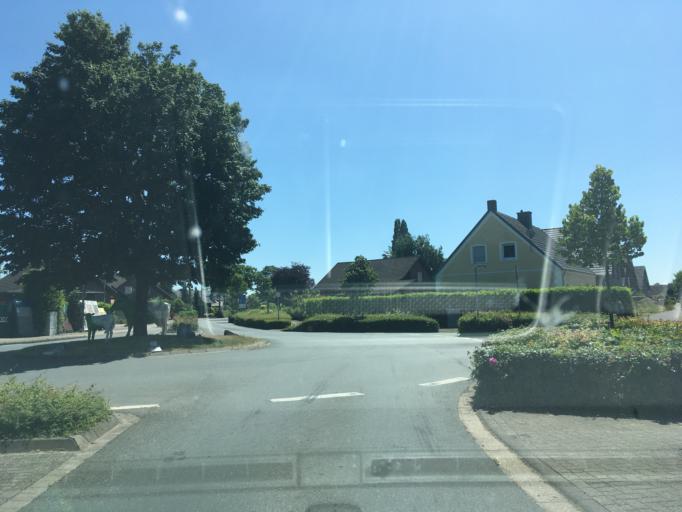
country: DE
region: North Rhine-Westphalia
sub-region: Regierungsbezirk Munster
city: Raesfeld
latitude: 51.7743
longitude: 6.8321
